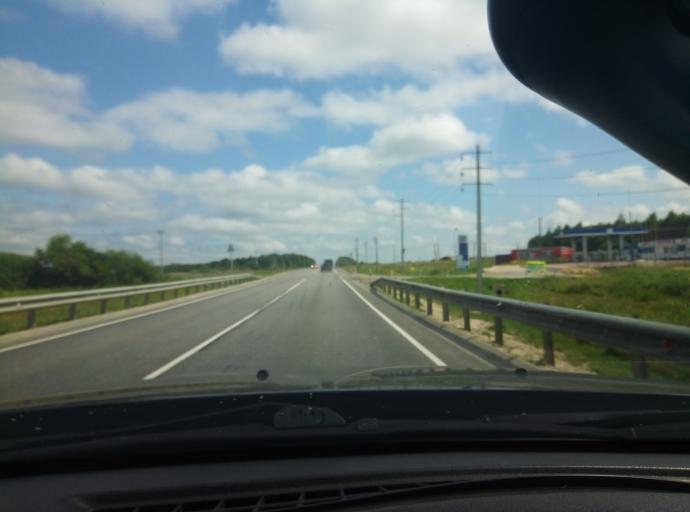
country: RU
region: Kaluga
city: Kaluga
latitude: 54.4337
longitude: 36.4089
